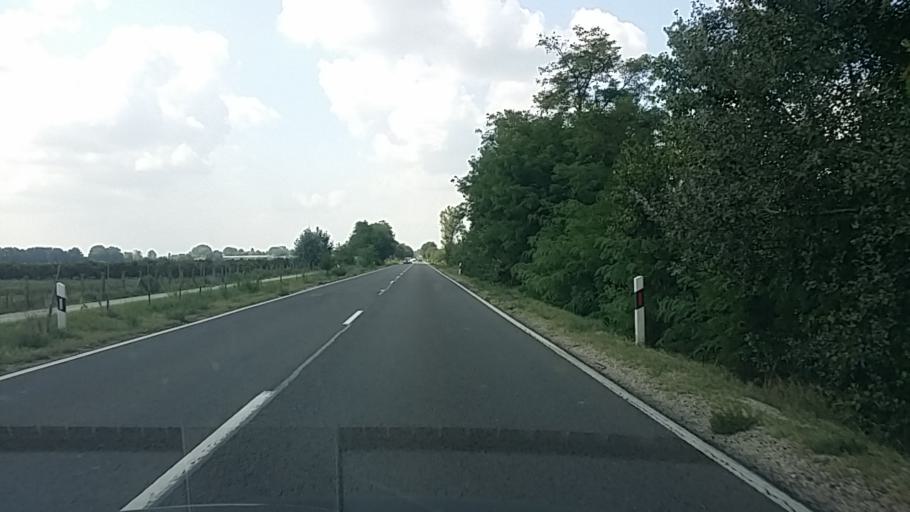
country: HU
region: Bacs-Kiskun
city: Nyarlorinc
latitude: 46.8657
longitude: 19.8993
